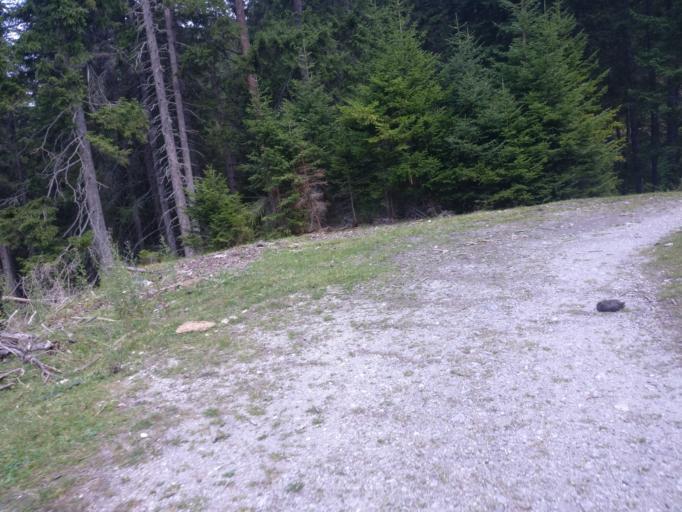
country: AT
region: Tyrol
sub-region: Politischer Bezirk Innsbruck Land
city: Mieders
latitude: 47.1423
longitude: 11.3895
